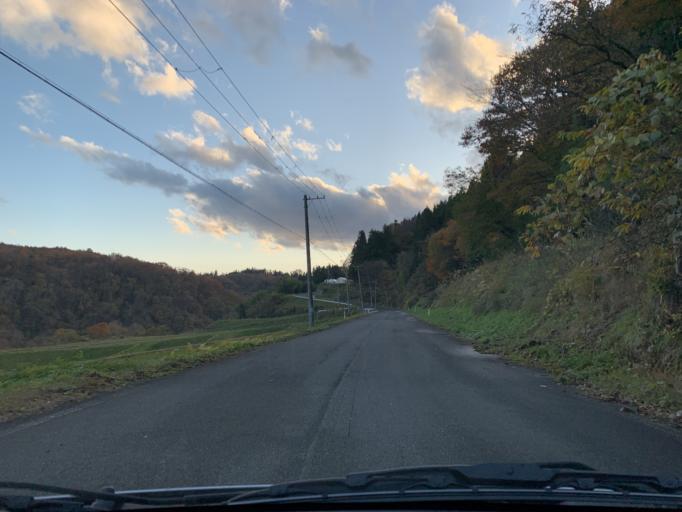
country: JP
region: Iwate
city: Mizusawa
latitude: 39.0289
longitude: 141.0374
